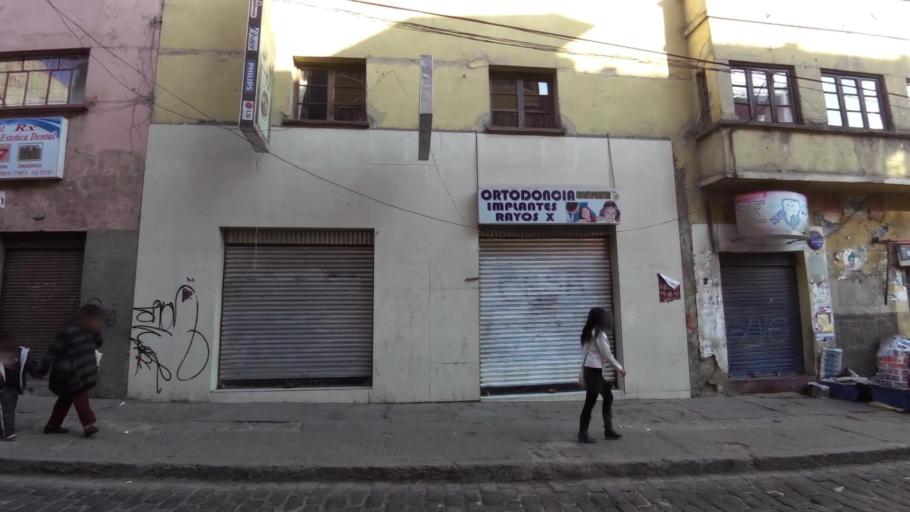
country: BO
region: La Paz
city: La Paz
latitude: -16.4989
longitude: -68.1444
